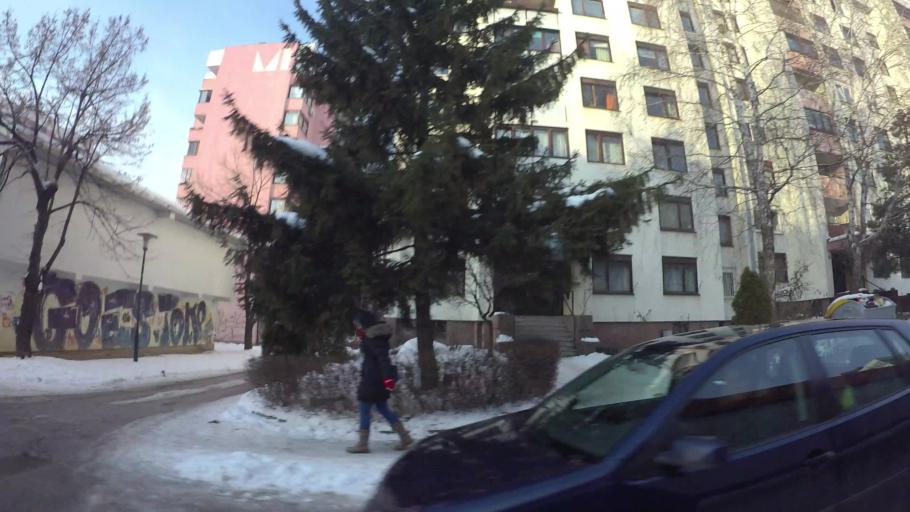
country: BA
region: Federation of Bosnia and Herzegovina
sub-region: Kanton Sarajevo
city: Sarajevo
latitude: 43.8384
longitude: 18.3466
